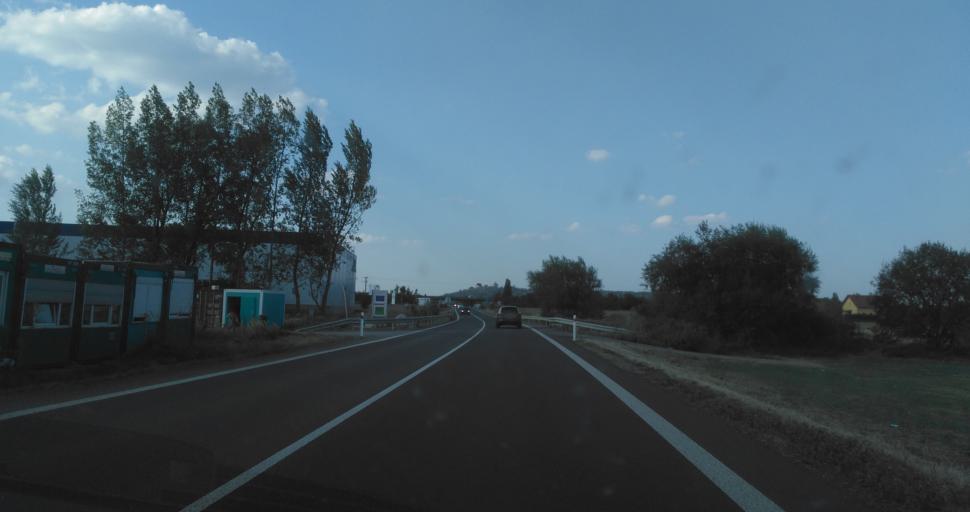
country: CZ
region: Central Bohemia
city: Zebrak
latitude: 49.8638
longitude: 13.8979
